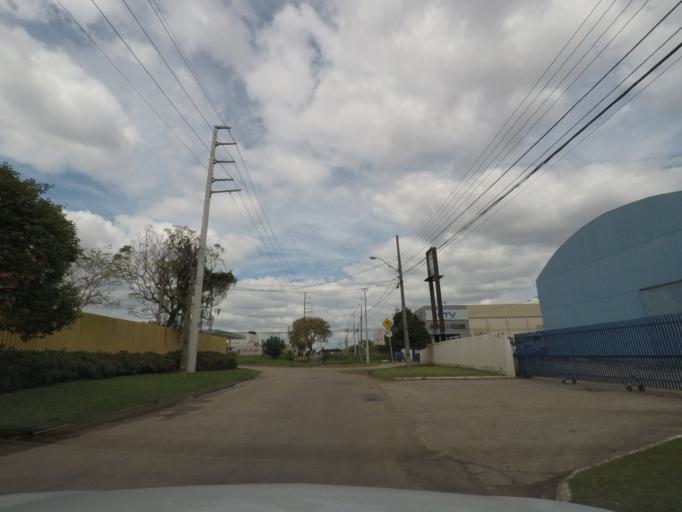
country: BR
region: Parana
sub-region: Sao Jose Dos Pinhais
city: Sao Jose dos Pinhais
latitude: -25.4915
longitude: -49.2313
